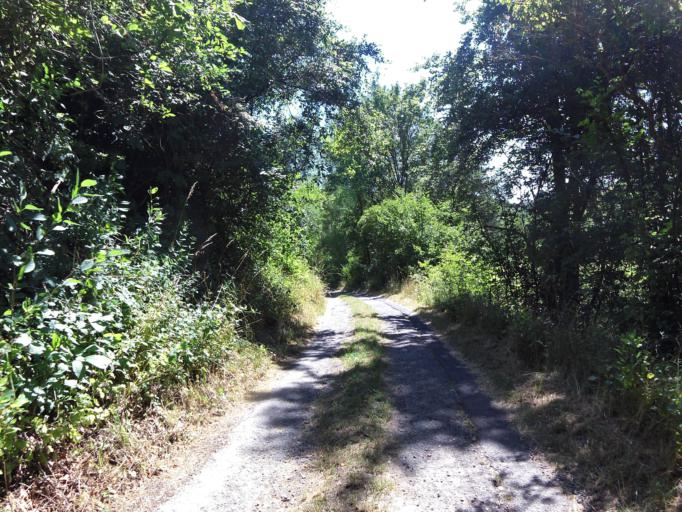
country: DE
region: Bavaria
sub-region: Regierungsbezirk Unterfranken
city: Randersacker
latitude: 49.7642
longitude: 9.9907
